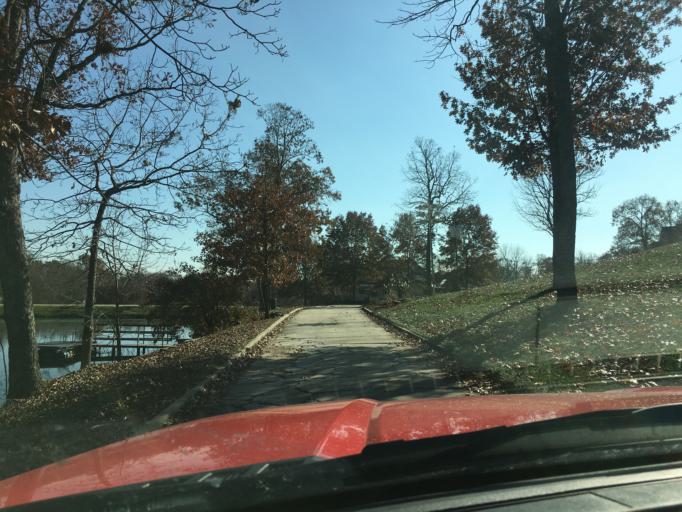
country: US
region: Missouri
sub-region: Cole County
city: Wardsville
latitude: 38.4825
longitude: -92.1820
